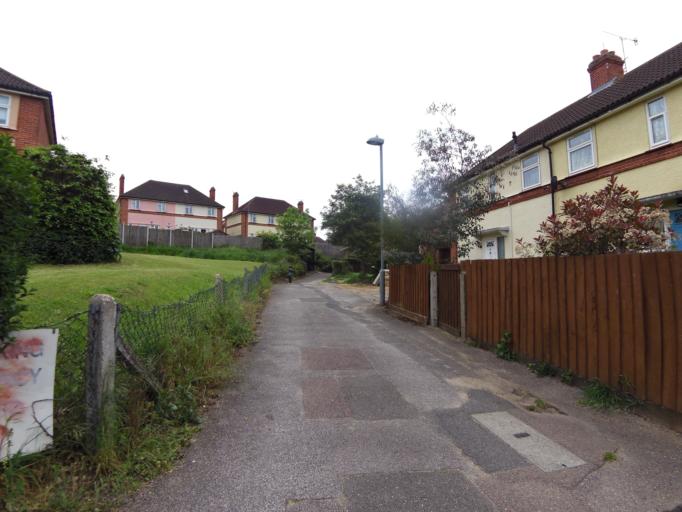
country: GB
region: England
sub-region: Suffolk
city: Ipswich
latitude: 52.0568
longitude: 1.1260
